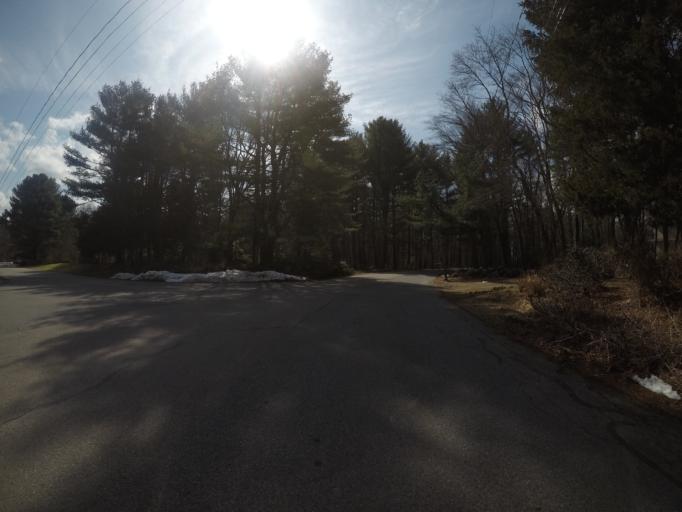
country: US
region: Massachusetts
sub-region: Bristol County
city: Easton
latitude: 42.0172
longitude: -71.1313
